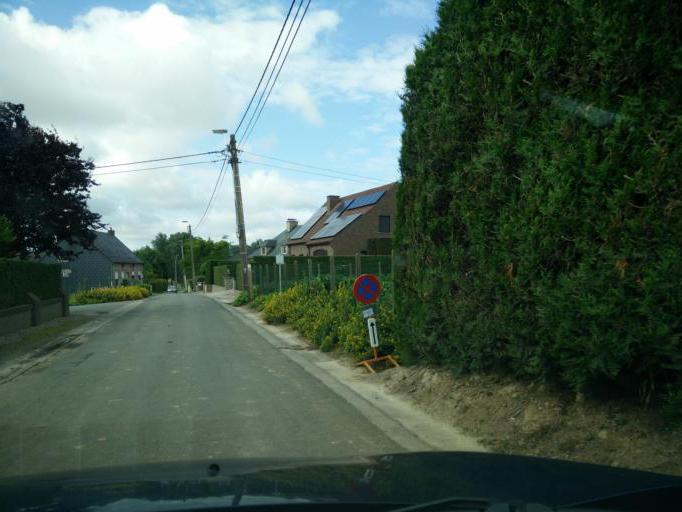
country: BE
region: Wallonia
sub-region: Province du Hainaut
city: Flobecq
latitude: 50.8018
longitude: 3.7447
